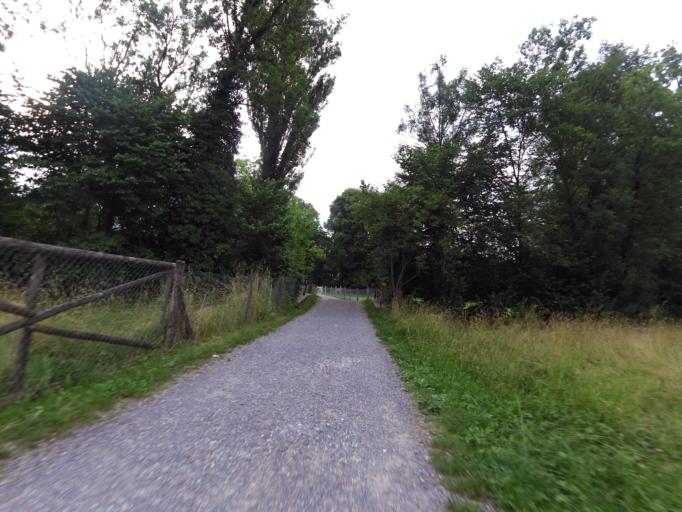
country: CH
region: Zurich
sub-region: Bezirk Dietikon
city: Schlieren / Engstingerquartier
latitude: 47.4074
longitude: 8.4406
